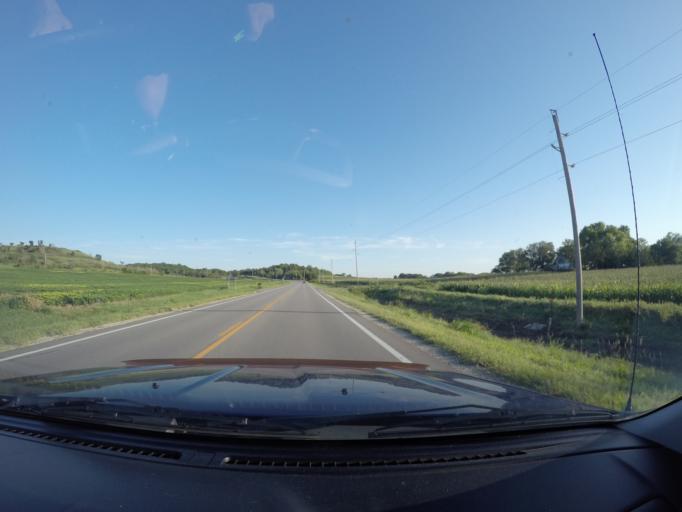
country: US
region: Kansas
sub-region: Pottawatomie County
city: Wamego
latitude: 39.1443
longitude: -96.3056
